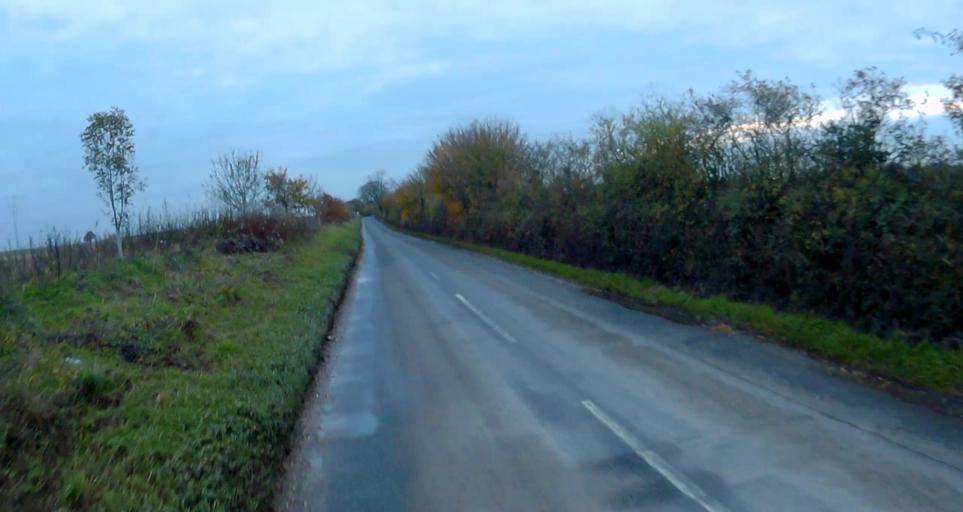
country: GB
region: England
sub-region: Hampshire
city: Odiham
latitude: 51.2530
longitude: -0.9614
